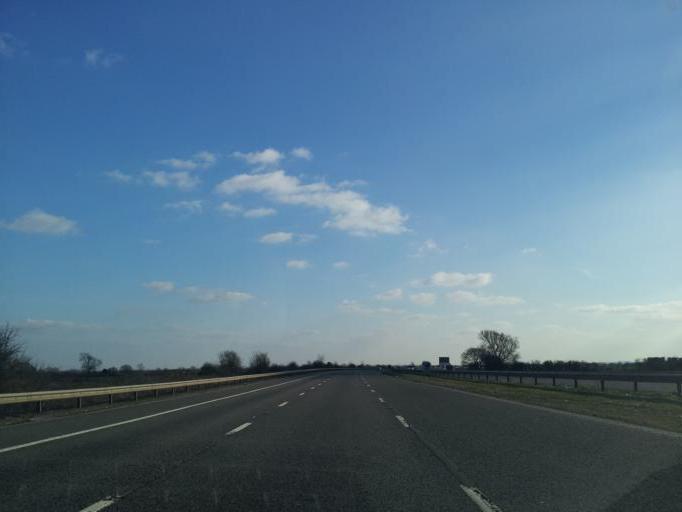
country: GB
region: England
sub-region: North Somerset
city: Bleadon
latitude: 51.2604
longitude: -2.9211
